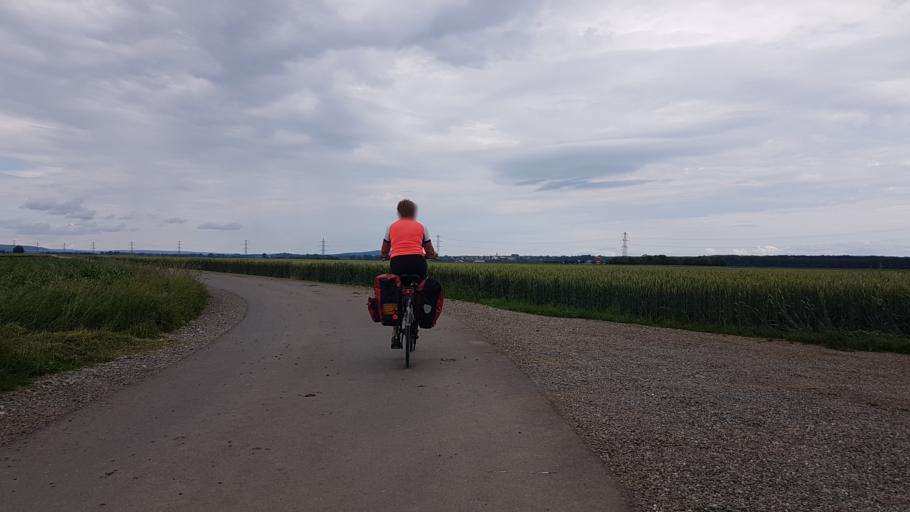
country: DE
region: Baden-Wuerttemberg
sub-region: Tuebingen Region
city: Herbertingen
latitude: 48.0789
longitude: 9.4167
